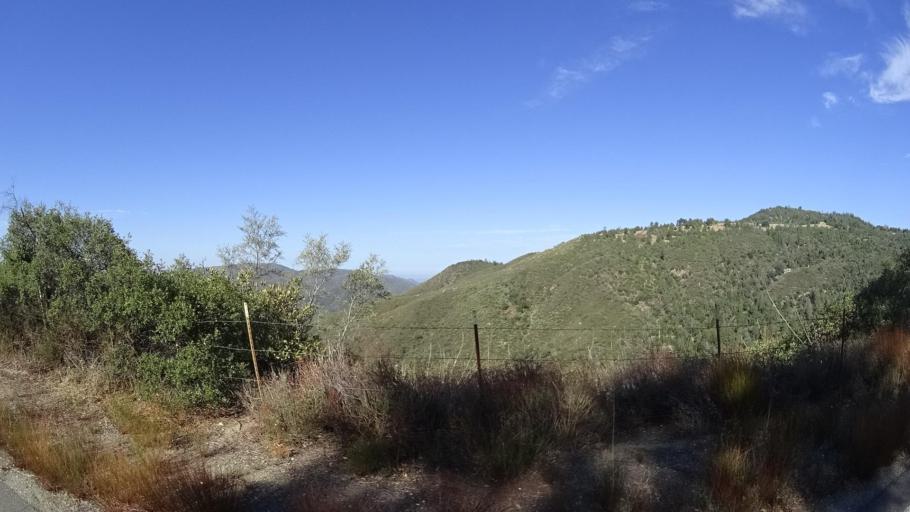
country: US
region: California
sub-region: Riverside County
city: Aguanga
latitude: 33.2715
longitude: -116.7831
